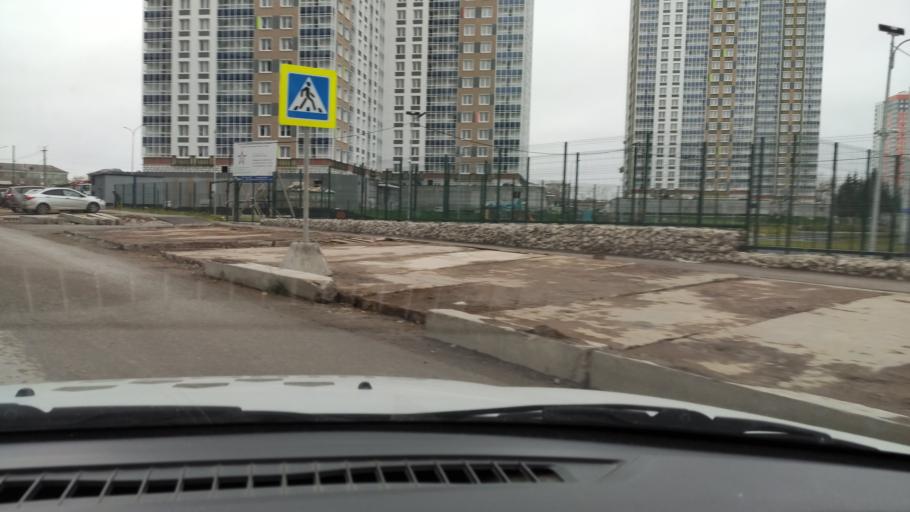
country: RU
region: Perm
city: Perm
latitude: 57.9911
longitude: 56.2646
